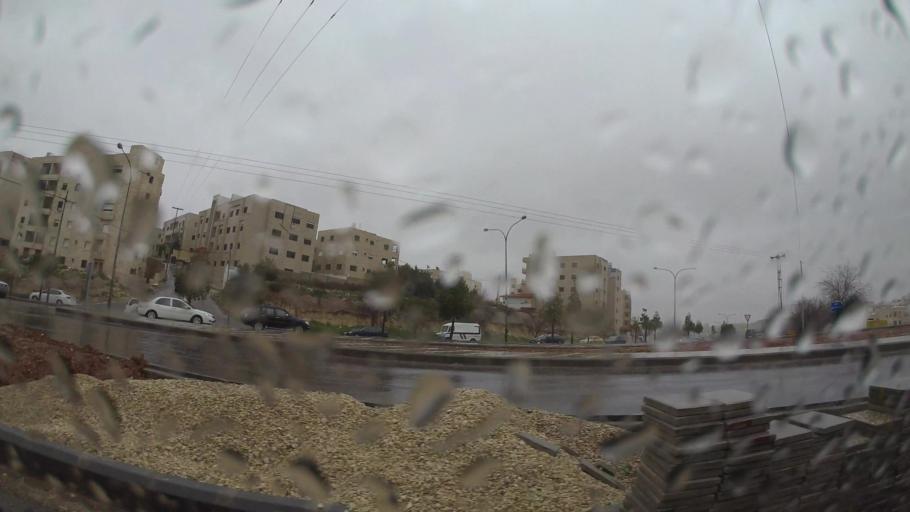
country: JO
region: Amman
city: Al Jubayhah
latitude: 32.0253
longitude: 35.8919
